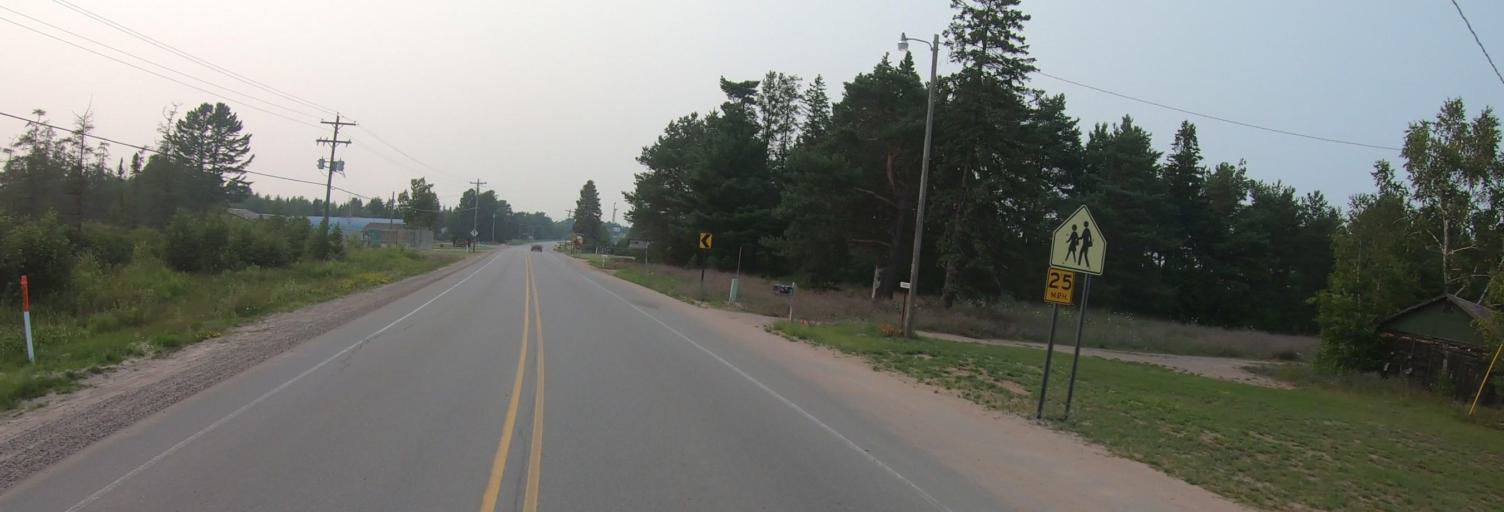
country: US
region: Michigan
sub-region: Chippewa County
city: Sault Ste. Marie
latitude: 46.4481
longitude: -84.5977
